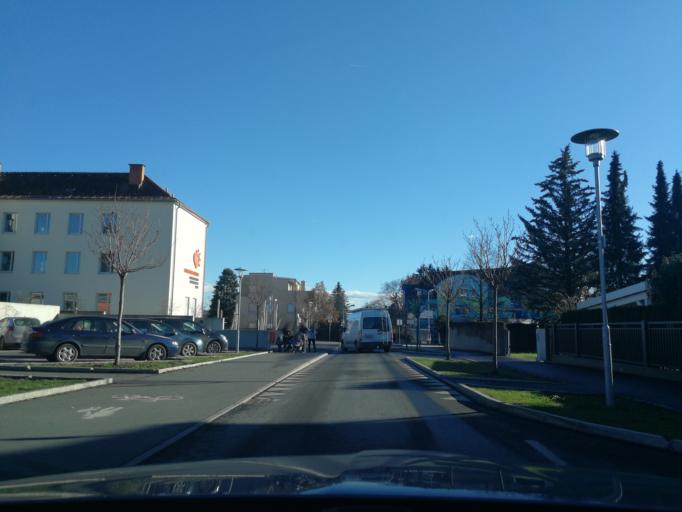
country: AT
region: Styria
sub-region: Politischer Bezirk Weiz
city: Gleisdorf
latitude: 47.1064
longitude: 15.7133
